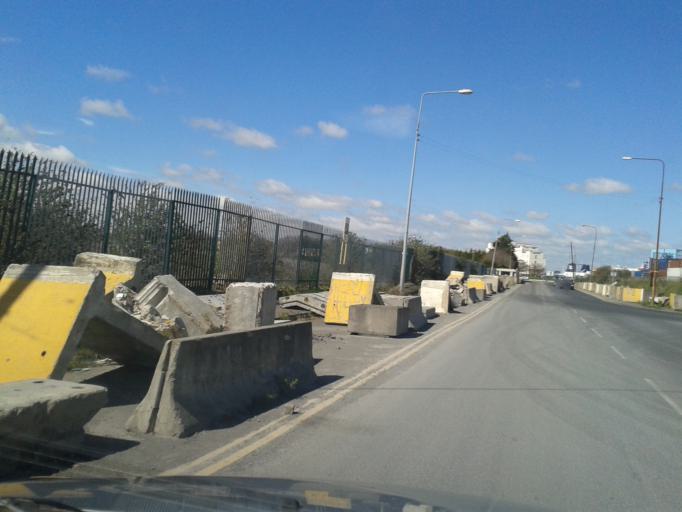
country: IE
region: Leinster
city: Sandymount
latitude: 53.3393
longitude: -6.2100
